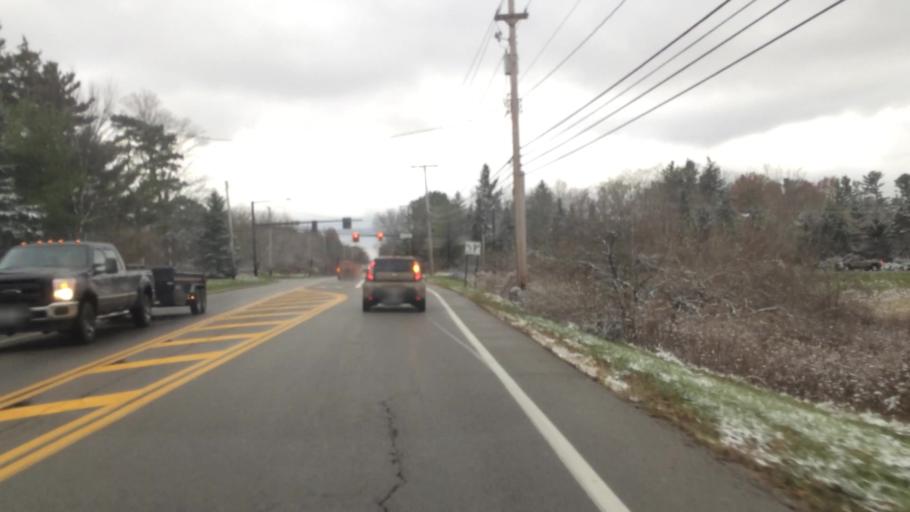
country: US
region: Ohio
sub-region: Summit County
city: Hudson
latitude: 41.2409
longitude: -81.4112
